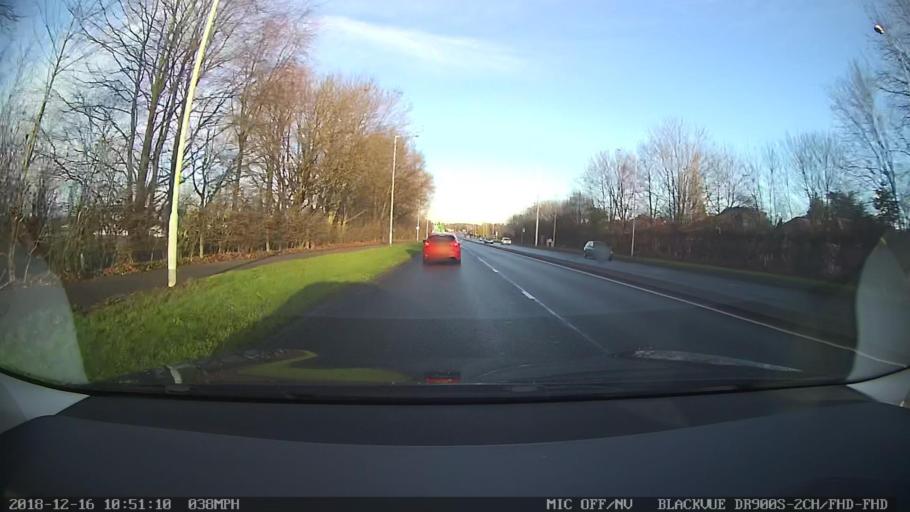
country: GB
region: England
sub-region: Manchester
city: Didsbury
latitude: 53.3860
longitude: -2.2239
